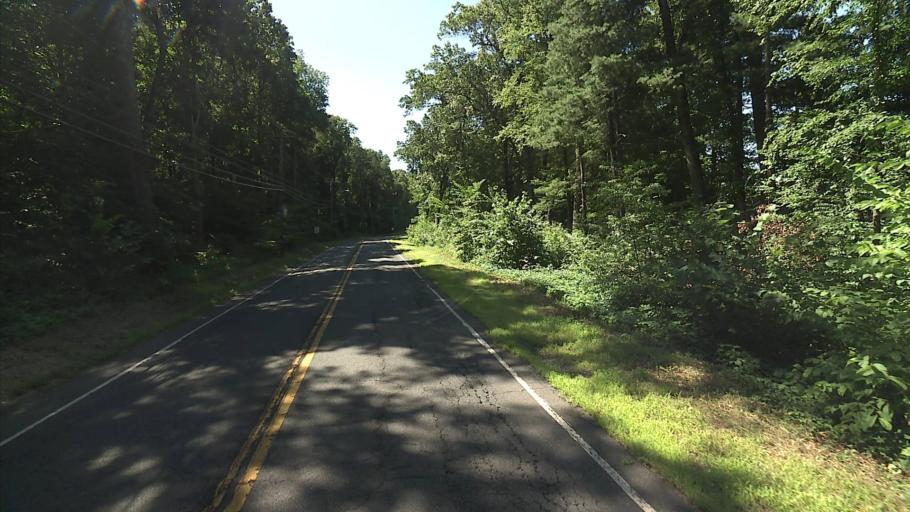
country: US
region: Connecticut
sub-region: Hartford County
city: Farmington
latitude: 41.7365
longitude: -72.8202
